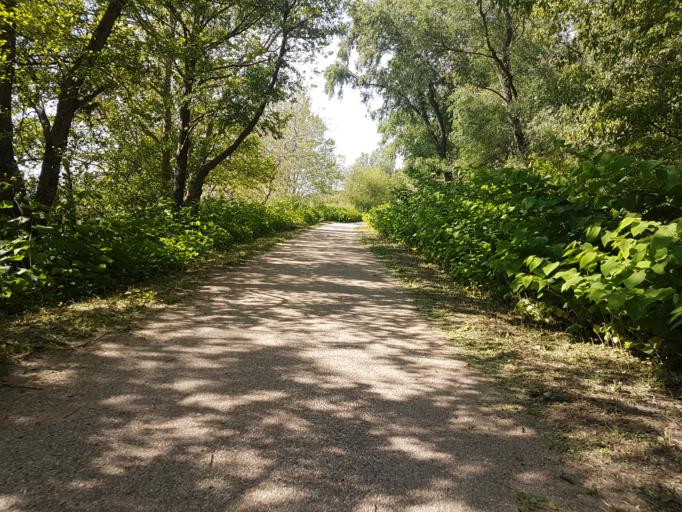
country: FR
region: Rhone-Alpes
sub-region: Departement de l'Ardeche
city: Beauchastel
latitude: 44.8104
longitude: 4.8008
